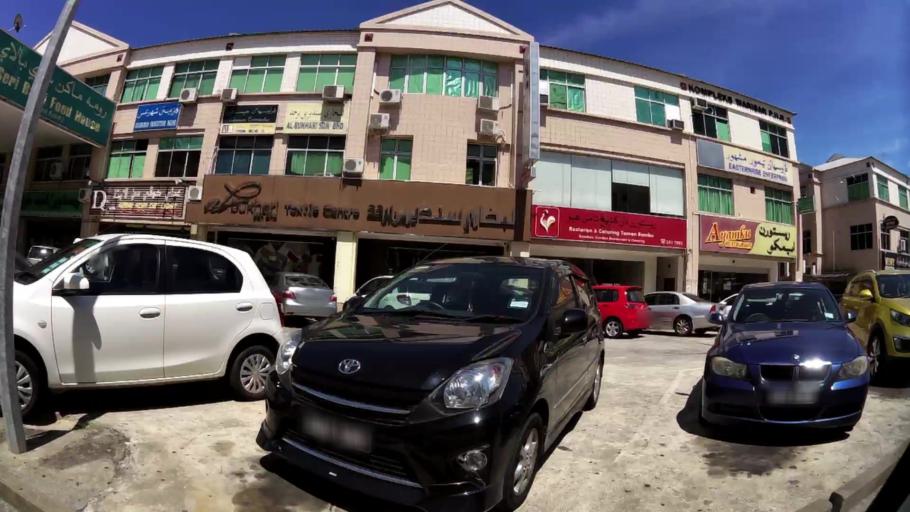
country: BN
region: Brunei and Muara
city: Bandar Seri Begawan
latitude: 4.9433
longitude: 114.9467
